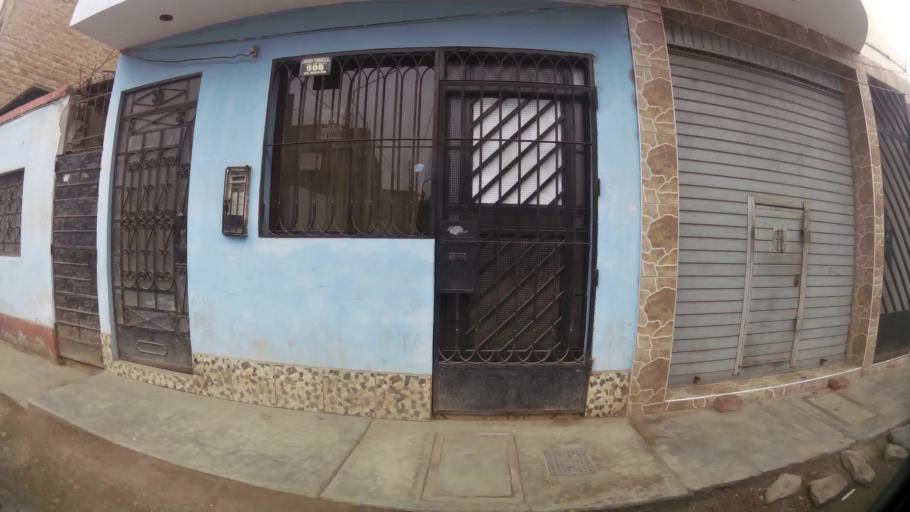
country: PE
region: Lima
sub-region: Provincia de Huaral
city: Huaral
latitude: -11.4998
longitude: -77.2034
